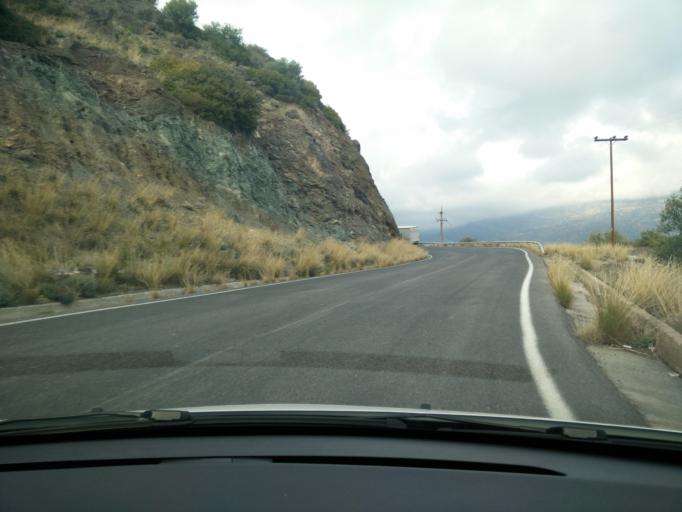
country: GR
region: Crete
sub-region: Nomos Lasithiou
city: Gra Liyia
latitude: 35.0207
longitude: 25.5759
